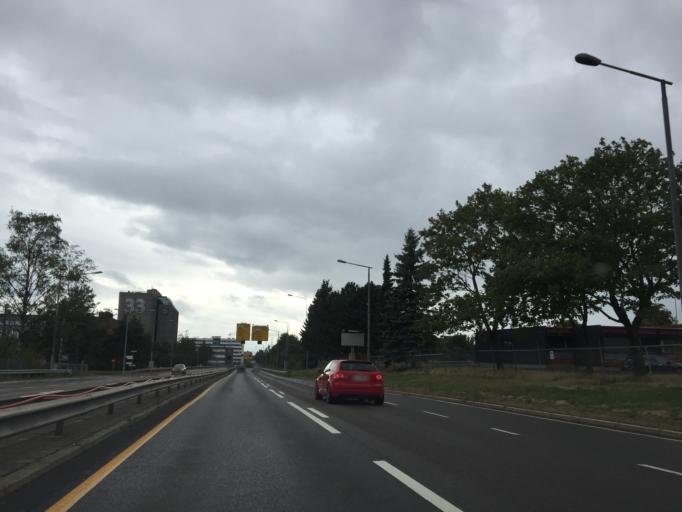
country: NO
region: Oslo
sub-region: Oslo
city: Oslo
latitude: 59.9308
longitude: 10.8226
